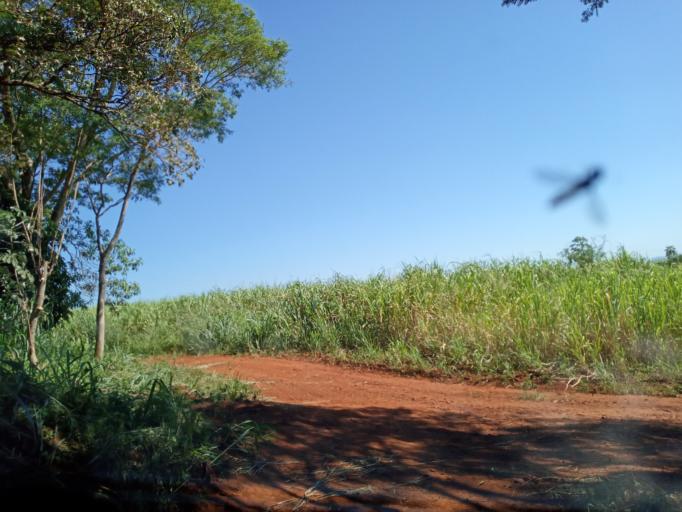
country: BR
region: Goias
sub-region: Itumbiara
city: Itumbiara
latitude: -18.4529
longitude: -49.1424
